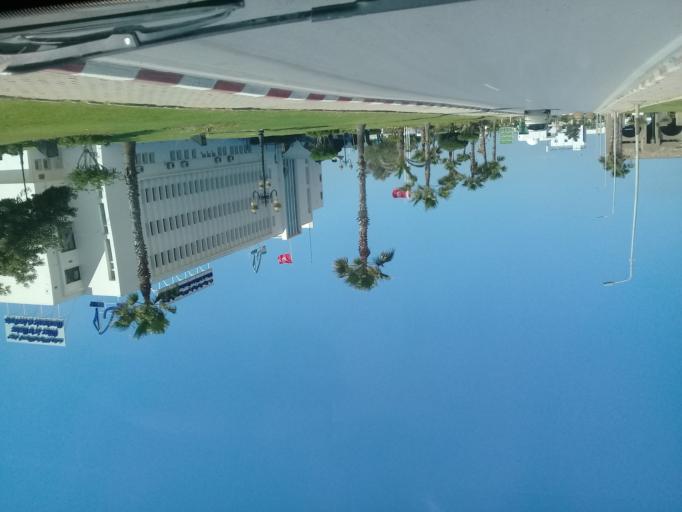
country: TN
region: Tunis
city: La Goulette
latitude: 36.8152
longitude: 10.2998
